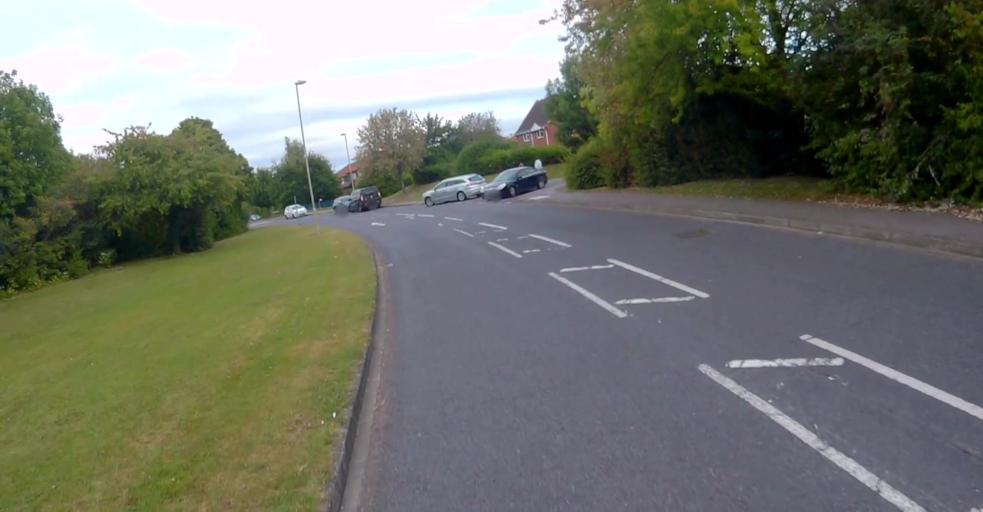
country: GB
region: England
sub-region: Hampshire
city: Basingstoke
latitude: 51.2410
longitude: -1.1242
